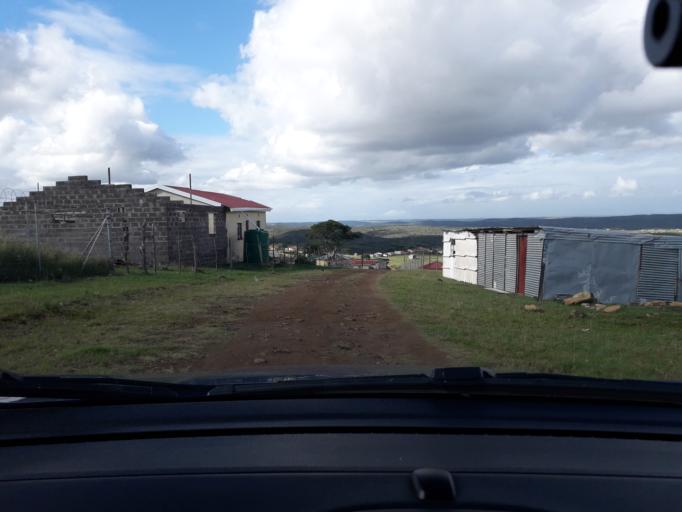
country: ZA
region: Eastern Cape
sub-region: Buffalo City Metropolitan Municipality
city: Bhisho
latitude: -33.1131
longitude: 27.4233
